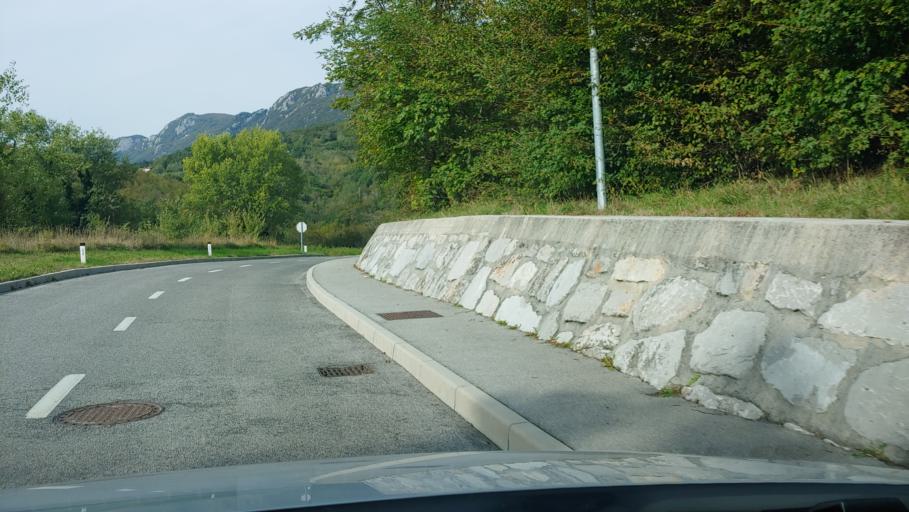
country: SI
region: Ajdovscina
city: Ajdovscina
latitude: 45.8993
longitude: 13.9067
